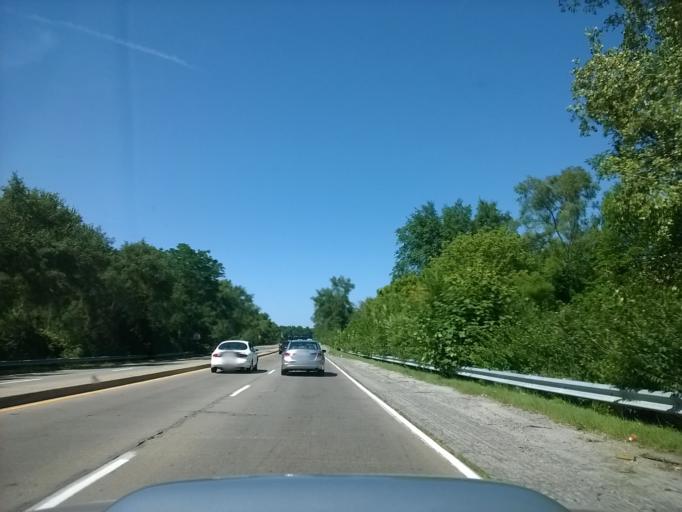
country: US
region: Indiana
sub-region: Marion County
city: Broad Ripple
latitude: 39.8942
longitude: -86.1218
